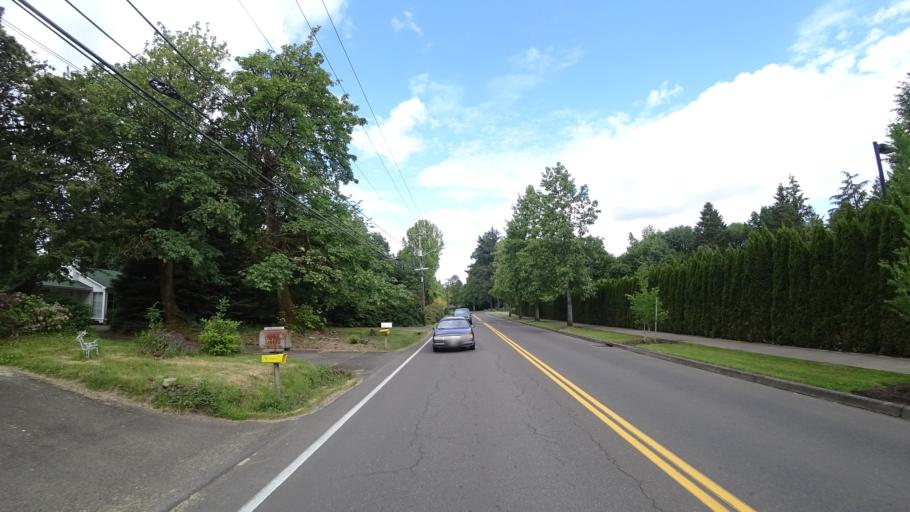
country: US
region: Oregon
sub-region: Clackamas County
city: Lake Oswego
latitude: 45.4518
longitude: -122.6734
